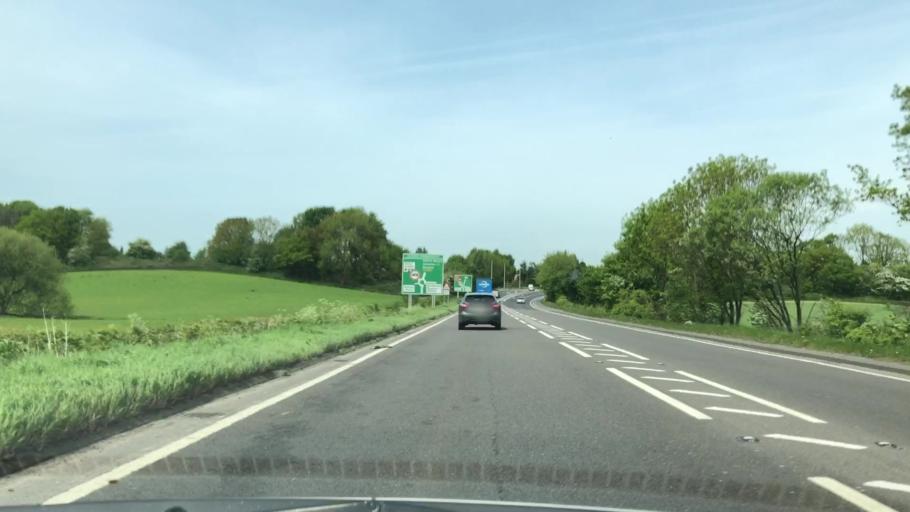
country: GB
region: England
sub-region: Shropshire
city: Gobowen
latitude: 52.9156
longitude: -3.0429
